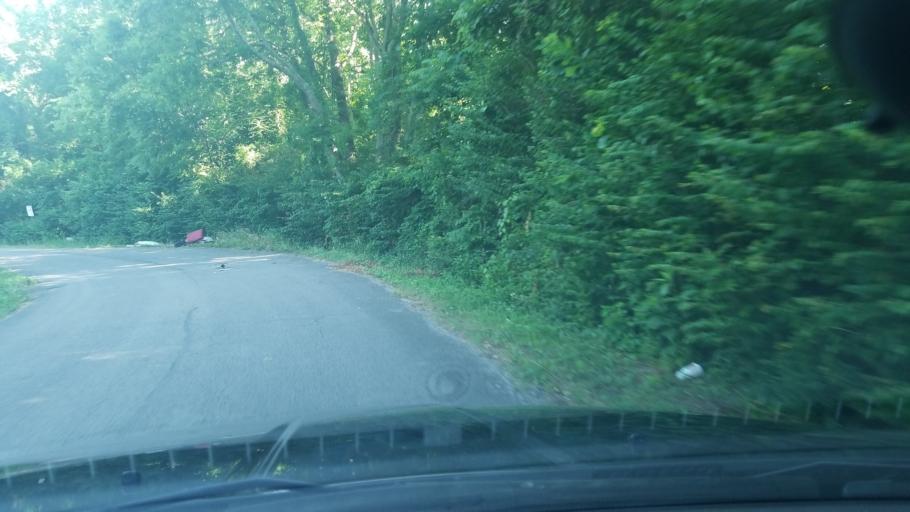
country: US
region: Tennessee
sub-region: Davidson County
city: Nashville
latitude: 36.2325
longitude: -86.7777
